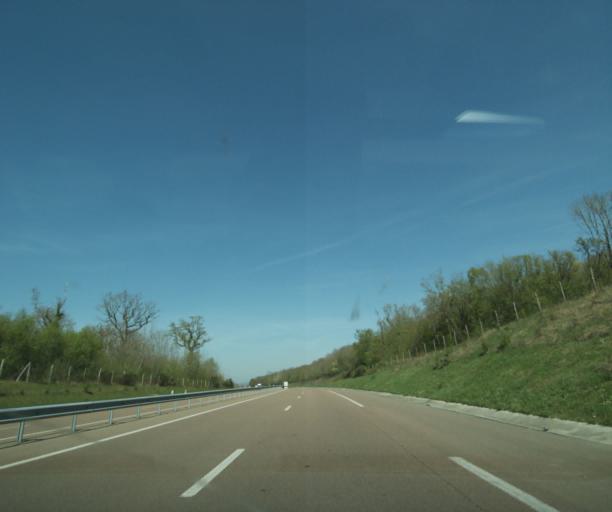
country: FR
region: Bourgogne
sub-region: Departement de la Nievre
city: Challuy
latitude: 46.9220
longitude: 3.1626
